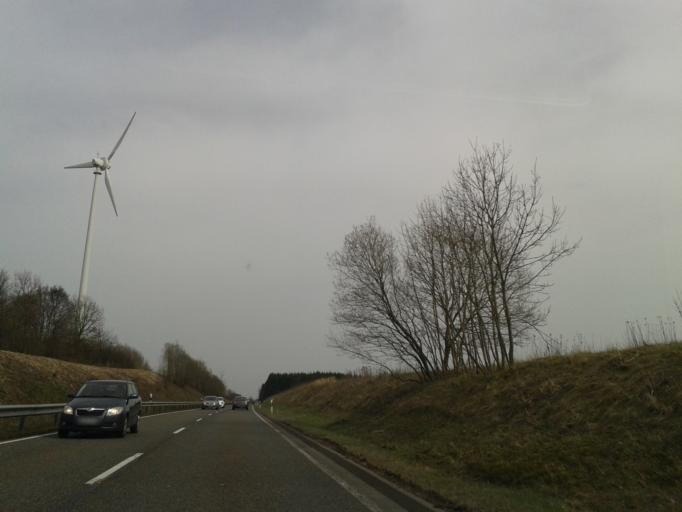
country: DE
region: Rheinland-Pfalz
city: Hof
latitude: 50.6646
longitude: 8.0267
